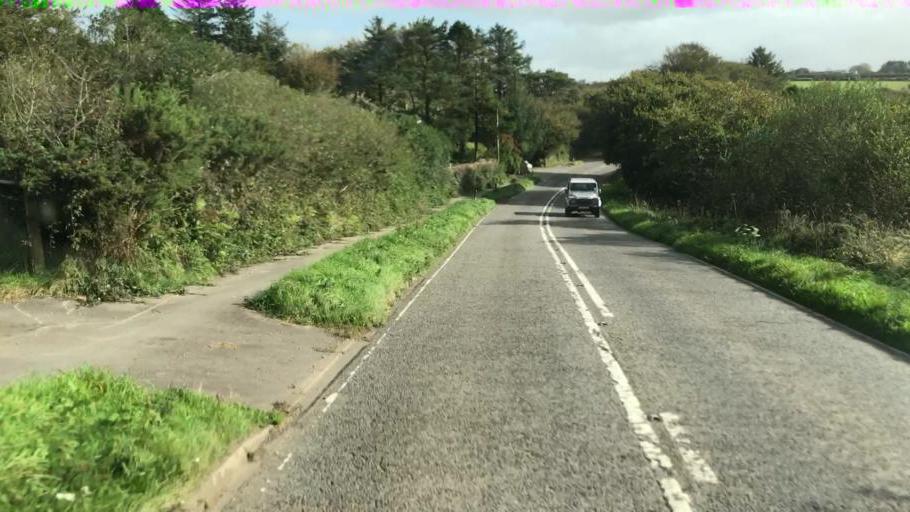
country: GB
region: England
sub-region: Cornwall
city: Callington
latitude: 50.5160
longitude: -4.2740
